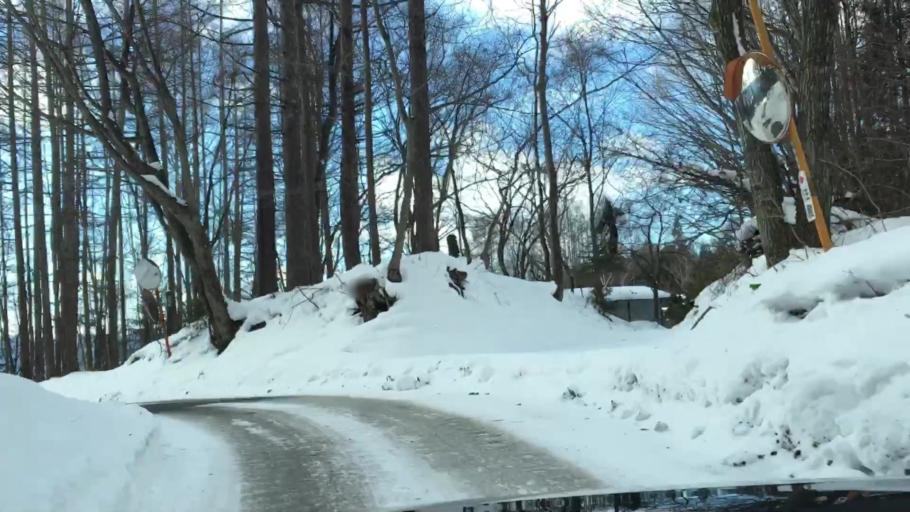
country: JP
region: Nagano
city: Nagano-shi
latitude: 36.7312
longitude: 138.0852
